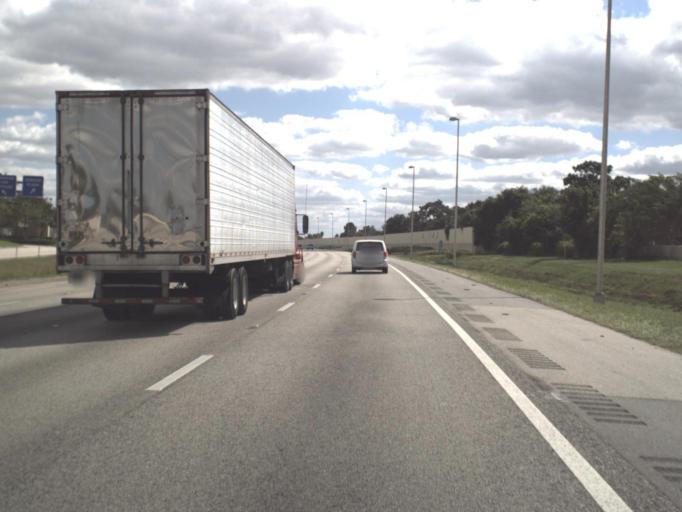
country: US
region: Florida
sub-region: Orange County
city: Gotha
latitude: 28.5163
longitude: -81.5031
